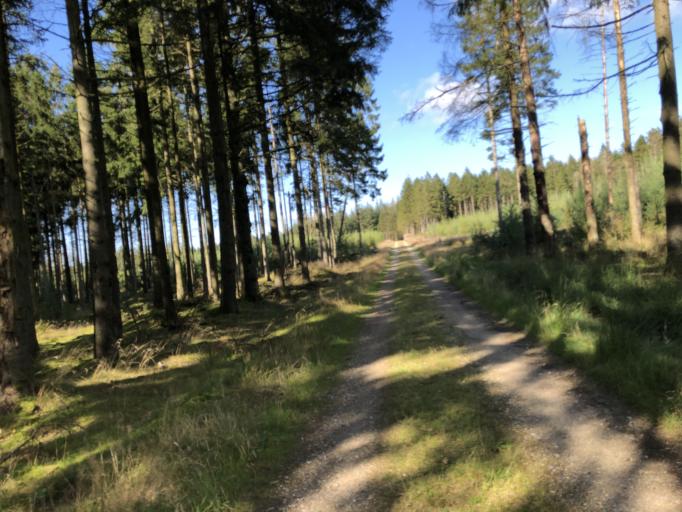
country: DK
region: Central Jutland
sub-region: Holstebro Kommune
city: Holstebro
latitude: 56.2460
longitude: 8.5017
